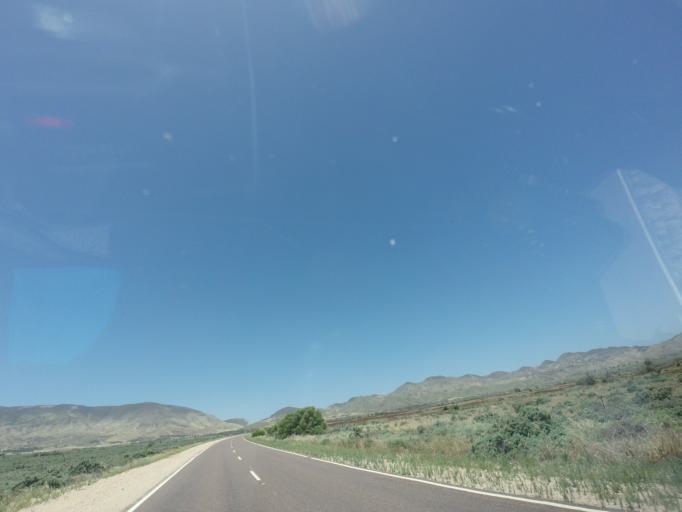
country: AU
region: South Australia
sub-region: Port Augusta
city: Port Augusta
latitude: -32.6174
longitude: 137.9789
